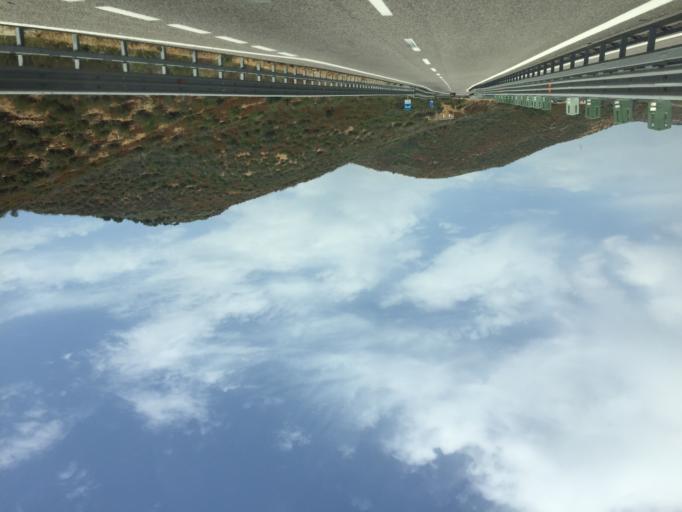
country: IT
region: Sardinia
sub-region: Provincia di Olbia-Tempio
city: San Teodoro
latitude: 40.7681
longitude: 9.6395
